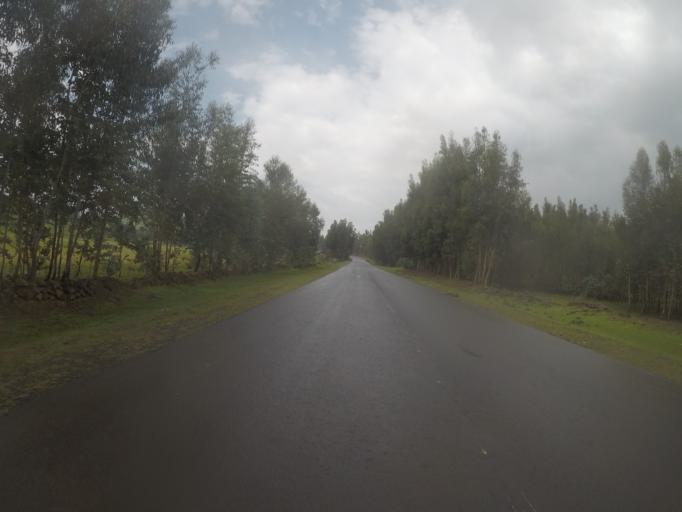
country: ET
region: Amhara
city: Debark'
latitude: 13.1088
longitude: 37.8622
